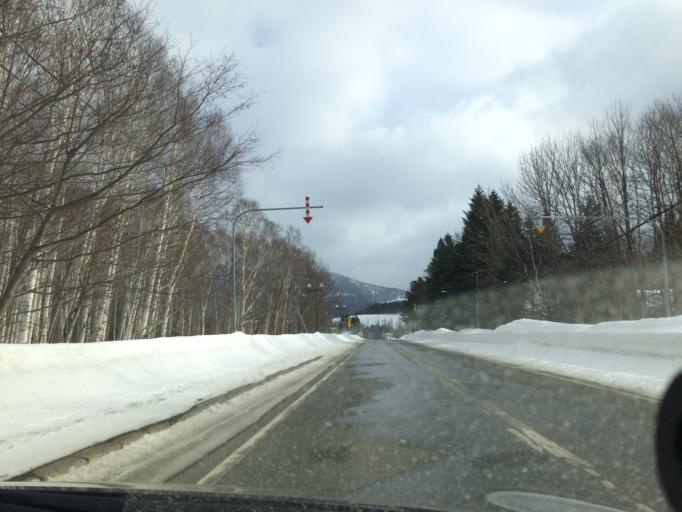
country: JP
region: Hokkaido
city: Shimo-furano
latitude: 43.0461
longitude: 142.6513
